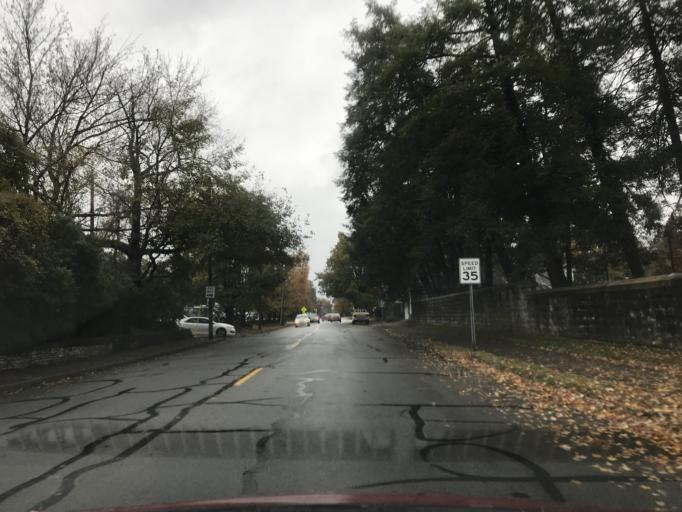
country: US
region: Kentucky
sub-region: Jefferson County
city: Audubon Park
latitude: 38.2346
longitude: -85.7198
